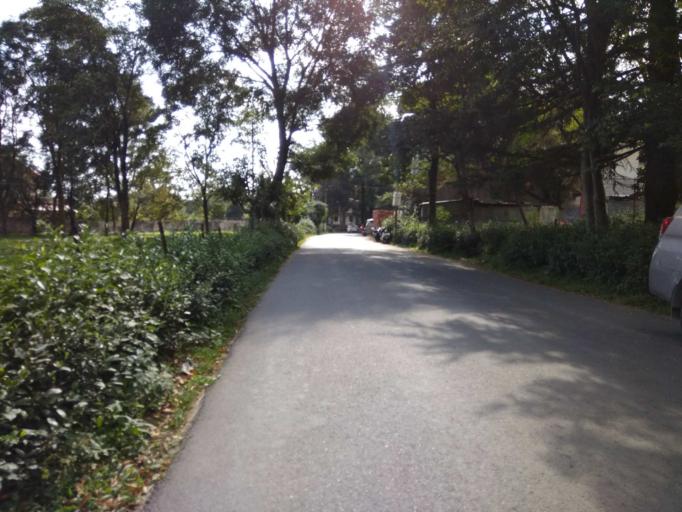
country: IN
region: Himachal Pradesh
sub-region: Kangra
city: Palampur
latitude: 32.1202
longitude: 76.5375
